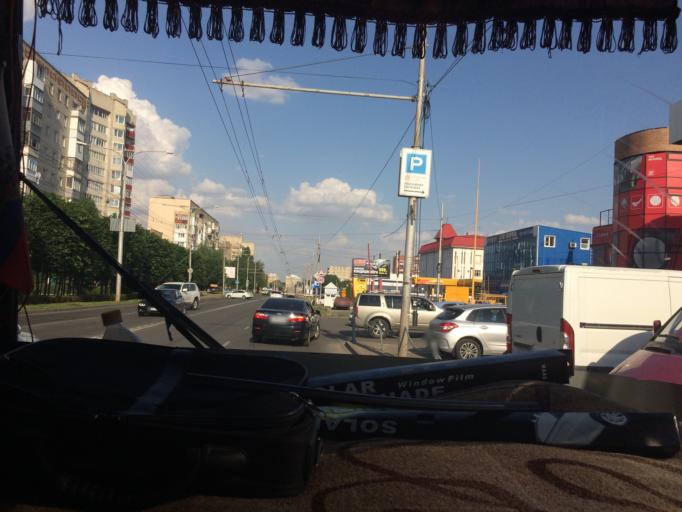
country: RU
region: Stavropol'skiy
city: Stavropol'
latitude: 45.0139
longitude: 41.9179
